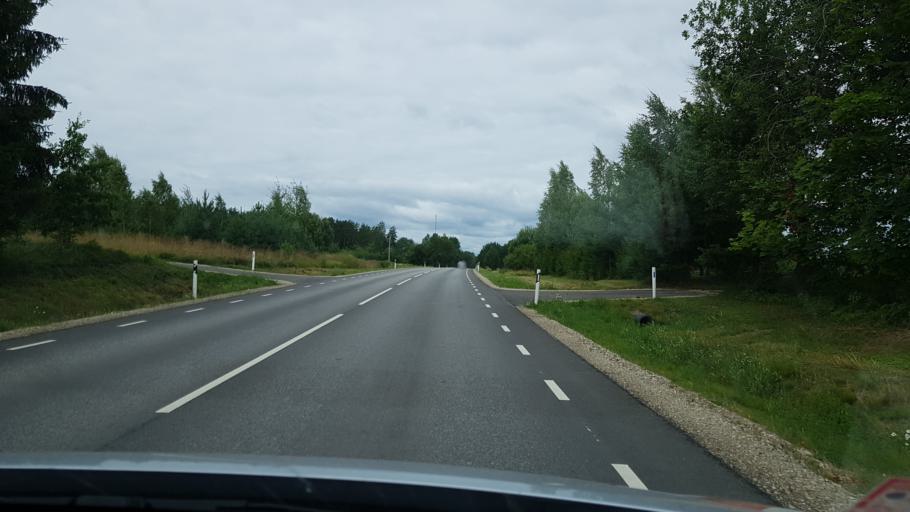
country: EE
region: Polvamaa
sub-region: Polva linn
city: Polva
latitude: 58.0108
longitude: 27.1834
